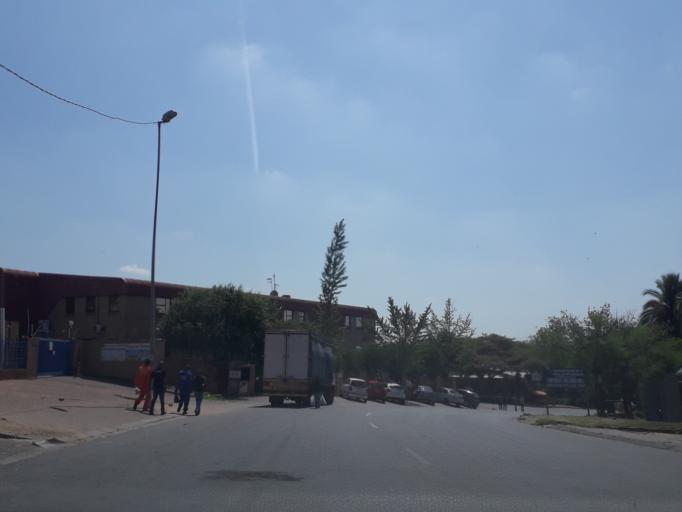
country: ZA
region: Gauteng
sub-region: West Rand District Municipality
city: Muldersdriseloop
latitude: -26.0283
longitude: 27.9507
